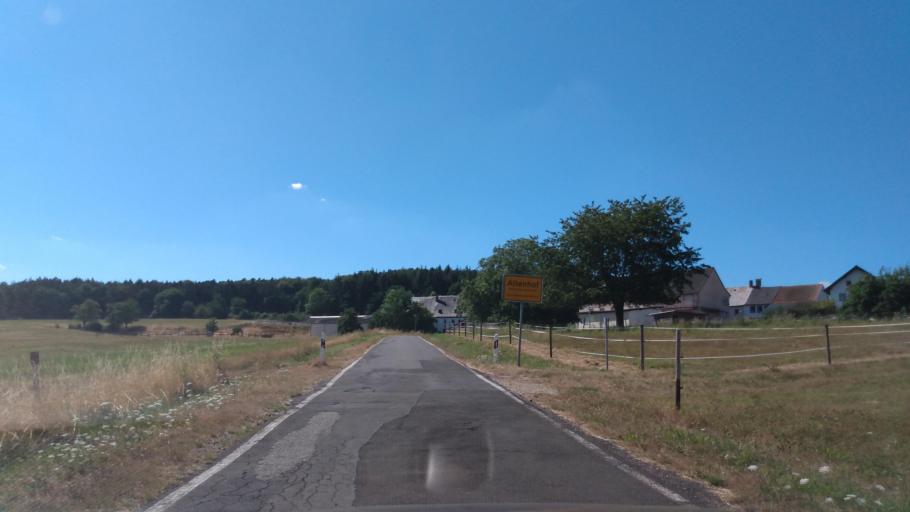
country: DE
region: Rheinland-Pfalz
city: Landscheid
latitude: 50.0159
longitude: 6.7572
